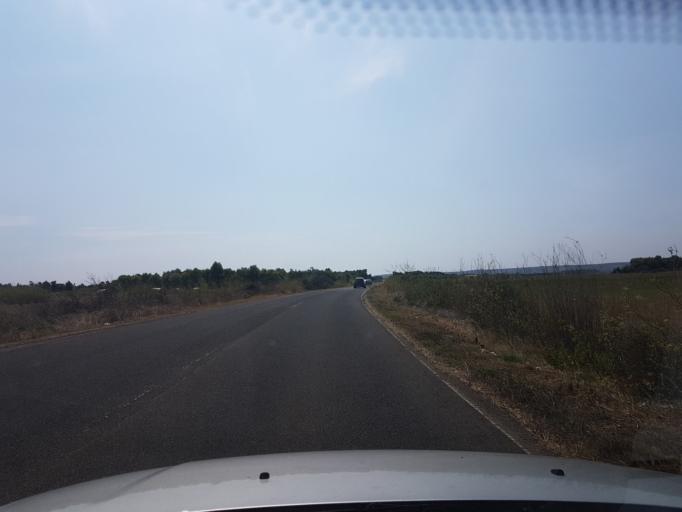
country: IT
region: Sardinia
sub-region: Provincia di Oristano
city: Cabras
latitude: 39.9176
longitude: 8.4908
